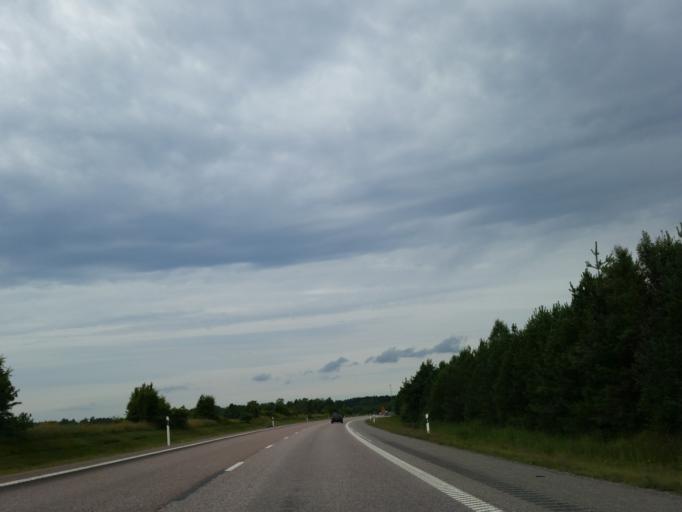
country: SE
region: Soedermanland
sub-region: Strangnas Kommun
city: Mariefred
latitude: 59.2167
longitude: 17.3049
